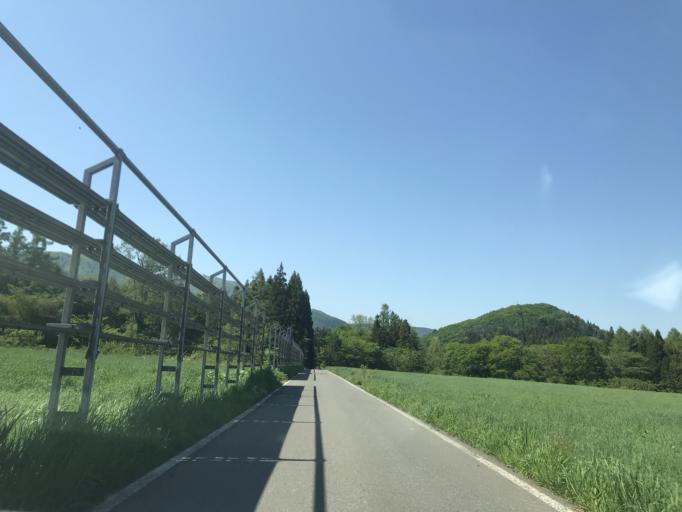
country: JP
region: Iwate
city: Shizukuishi
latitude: 39.5616
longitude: 140.8320
